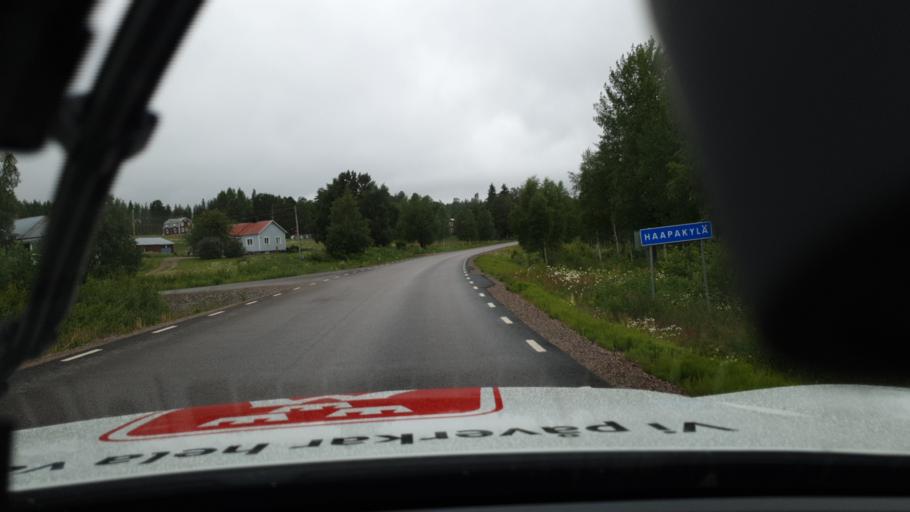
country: SE
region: Norrbotten
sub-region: Overtornea Kommun
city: OEvertornea
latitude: 66.3996
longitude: 23.6150
